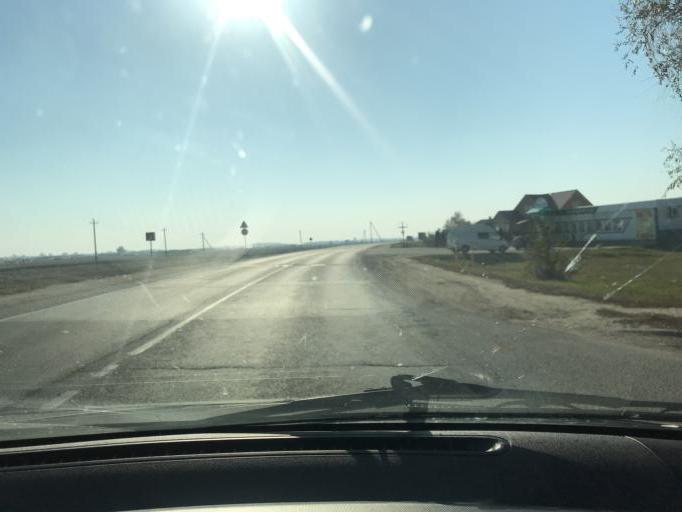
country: BY
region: Brest
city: Davyd-Haradok
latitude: 52.0683
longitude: 27.3371
